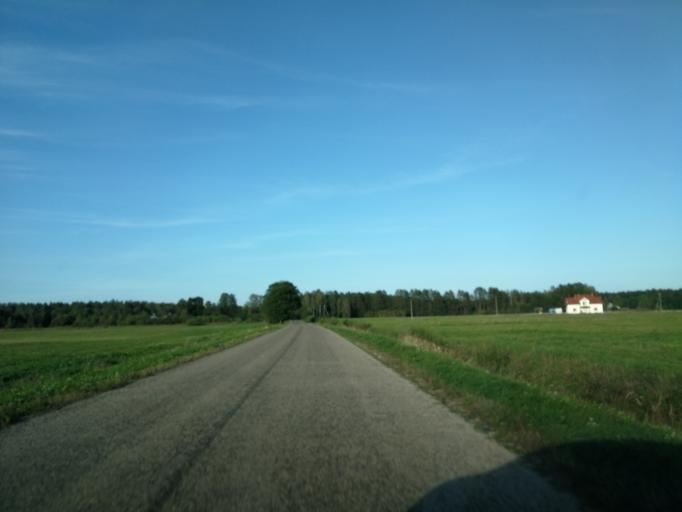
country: LV
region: Garkalne
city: Garkalne
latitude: 57.0758
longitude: 24.4461
